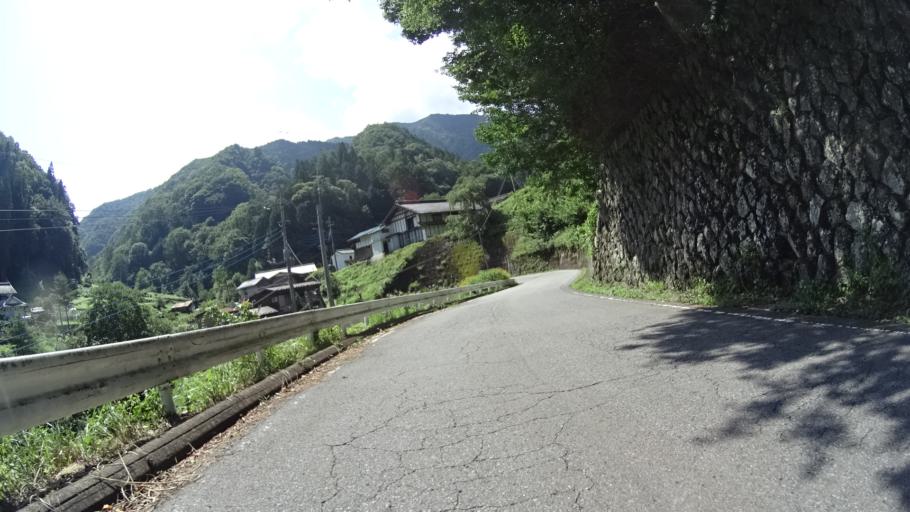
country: JP
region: Gunma
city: Tomioka
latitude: 36.0641
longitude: 138.8326
